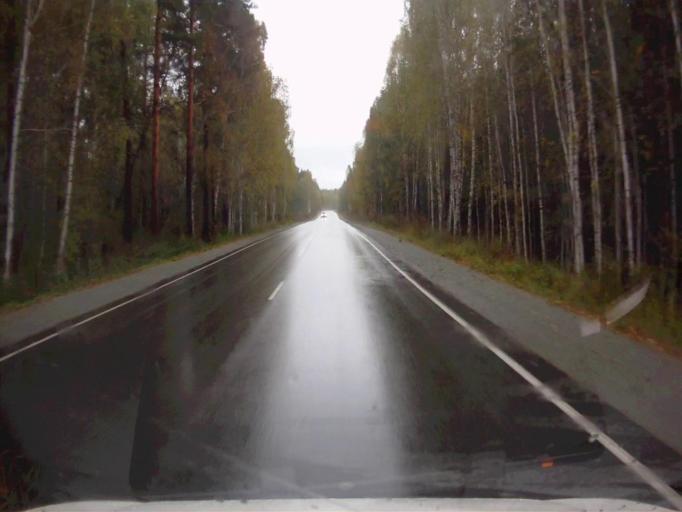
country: RU
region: Chelyabinsk
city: Kyshtym
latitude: 55.6496
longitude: 60.5811
